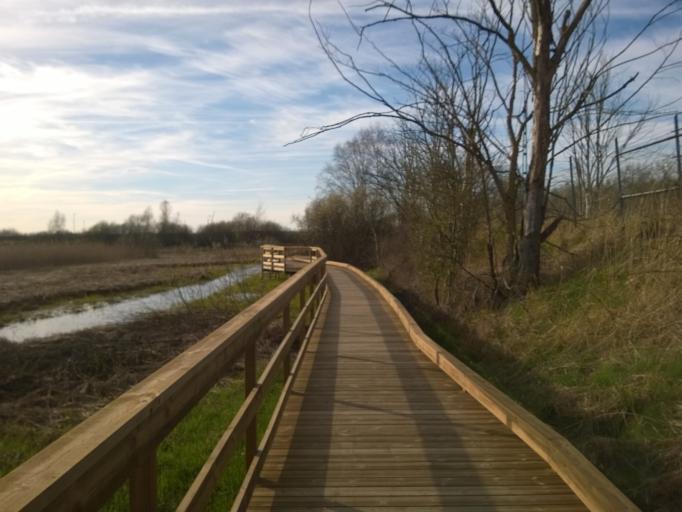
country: SE
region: Skane
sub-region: Kristianstads Kommun
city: Kristianstad
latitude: 56.0358
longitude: 14.1447
